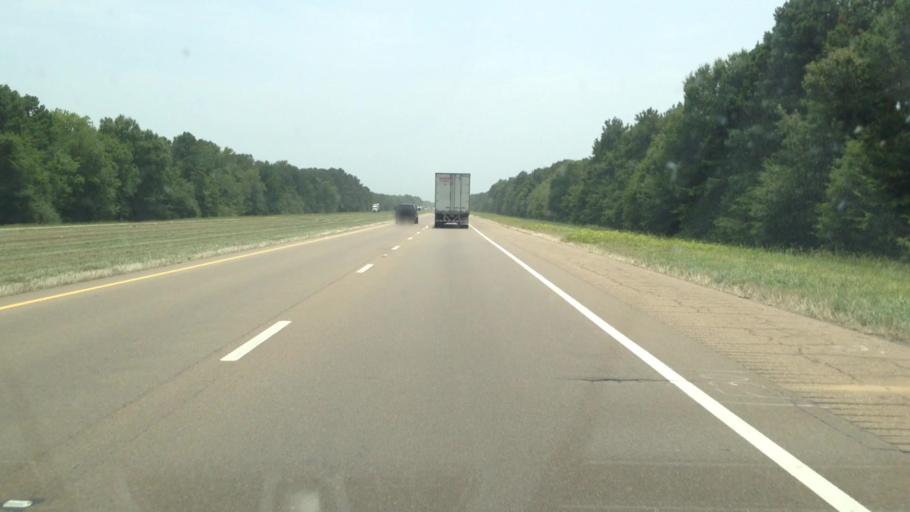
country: US
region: Texas
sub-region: Morris County
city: Naples
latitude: 33.3467
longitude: -94.6557
